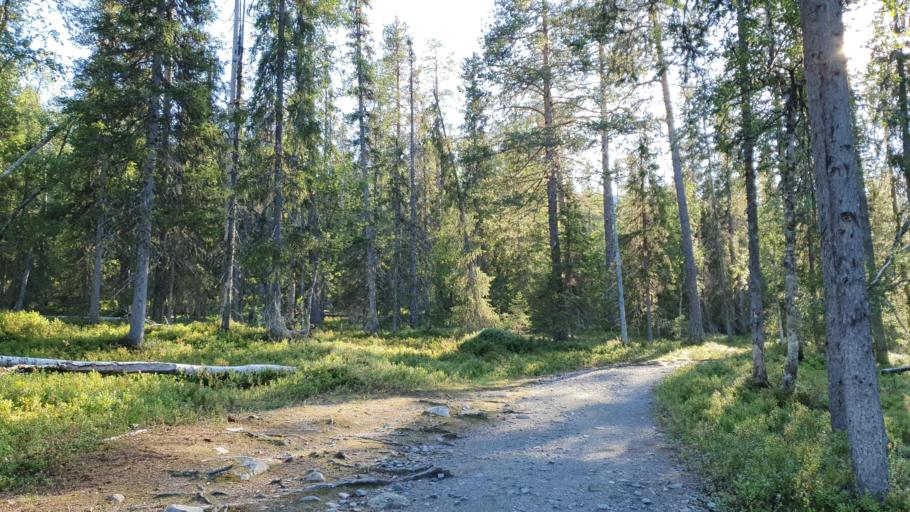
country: FI
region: Lapland
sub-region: Tunturi-Lappi
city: Kolari
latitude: 67.5963
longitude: 24.2538
